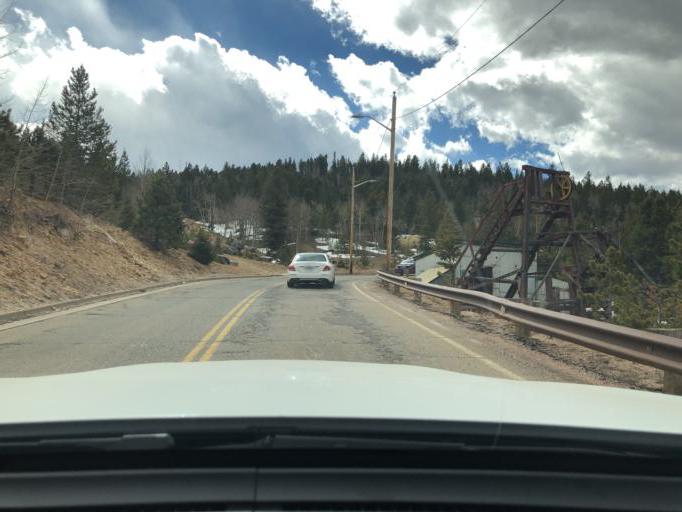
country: US
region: Colorado
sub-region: Gilpin County
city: Central City
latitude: 39.7948
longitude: -105.5121
